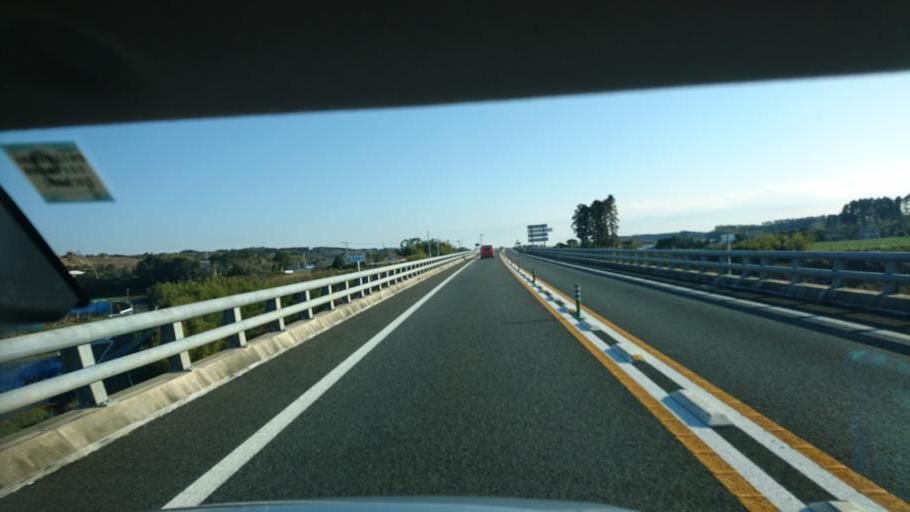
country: JP
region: Miyazaki
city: Takanabe
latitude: 32.1315
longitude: 131.4697
